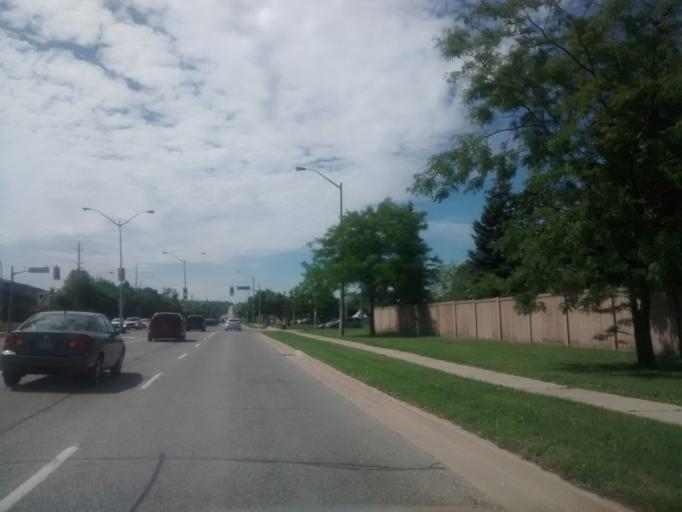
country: CA
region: Ontario
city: Burlington
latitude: 43.3747
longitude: -79.8355
